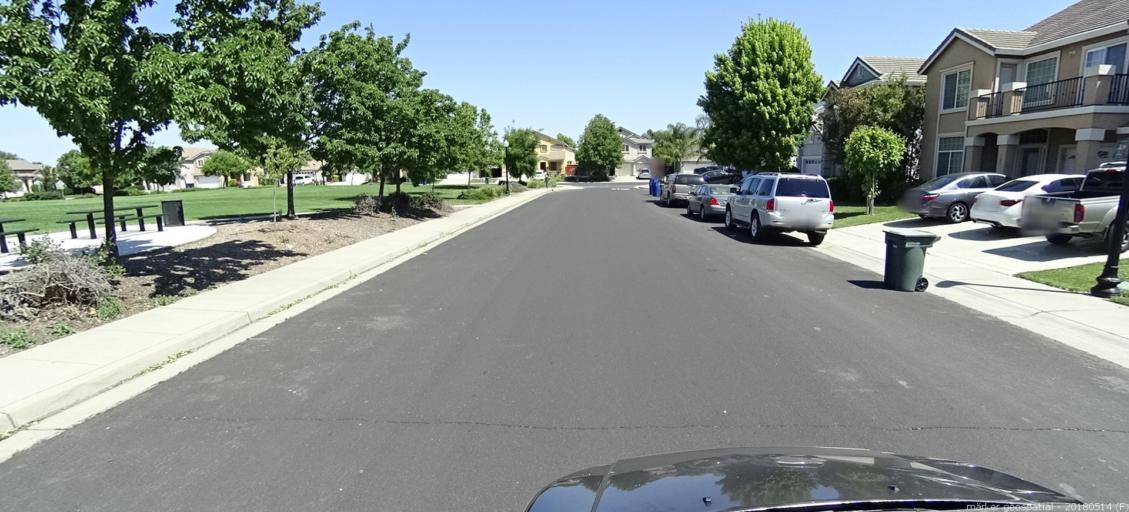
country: US
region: California
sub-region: Yolo County
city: West Sacramento
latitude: 38.6301
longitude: -121.5271
